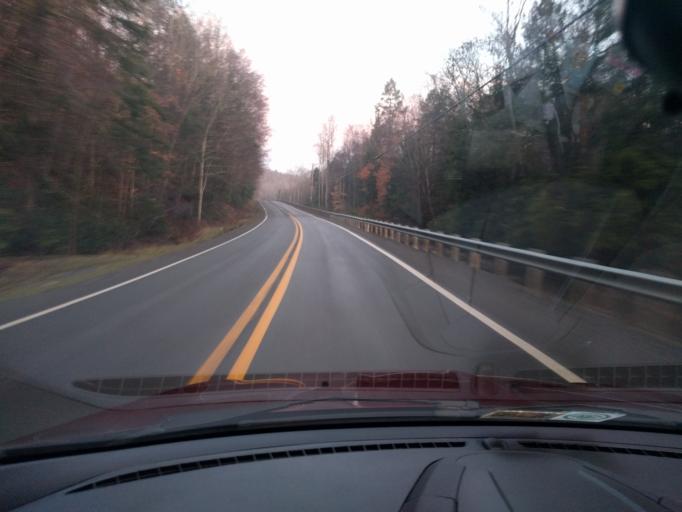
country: US
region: West Virginia
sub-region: Greenbrier County
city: Rainelle
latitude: 38.0358
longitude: -80.9183
